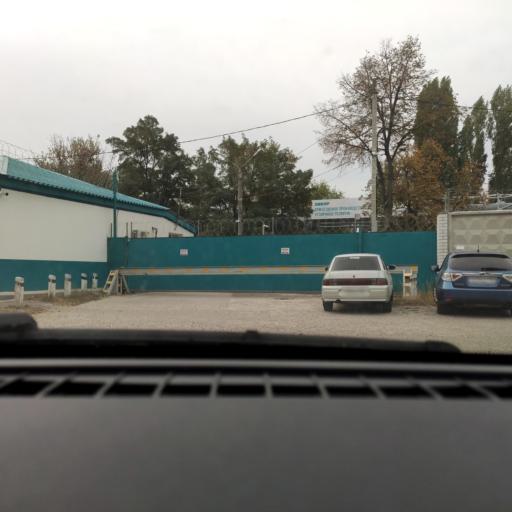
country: RU
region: Voronezj
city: Voronezh
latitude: 51.6298
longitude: 39.2374
